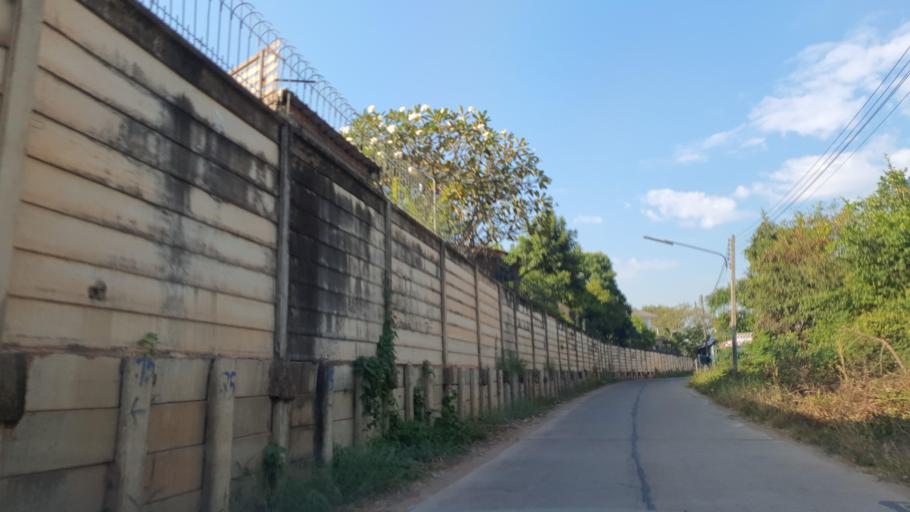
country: TH
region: Khon Kaen
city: Khon Kaen
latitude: 16.4149
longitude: 102.8134
